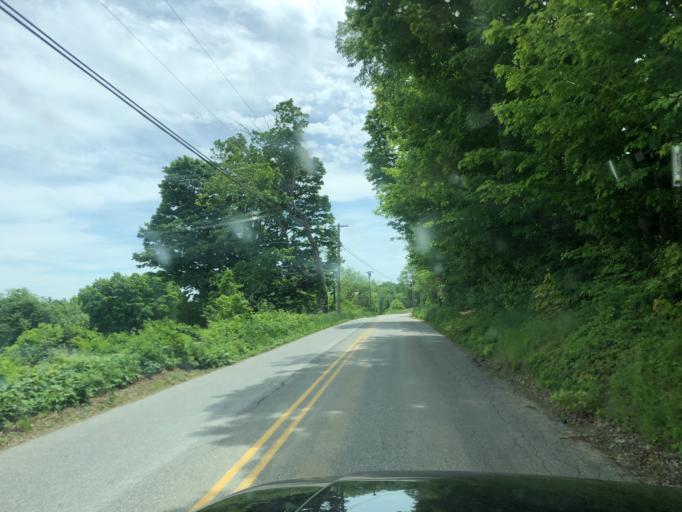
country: US
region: Connecticut
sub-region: Windham County
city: Thompson
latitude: 41.9693
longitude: -71.8346
